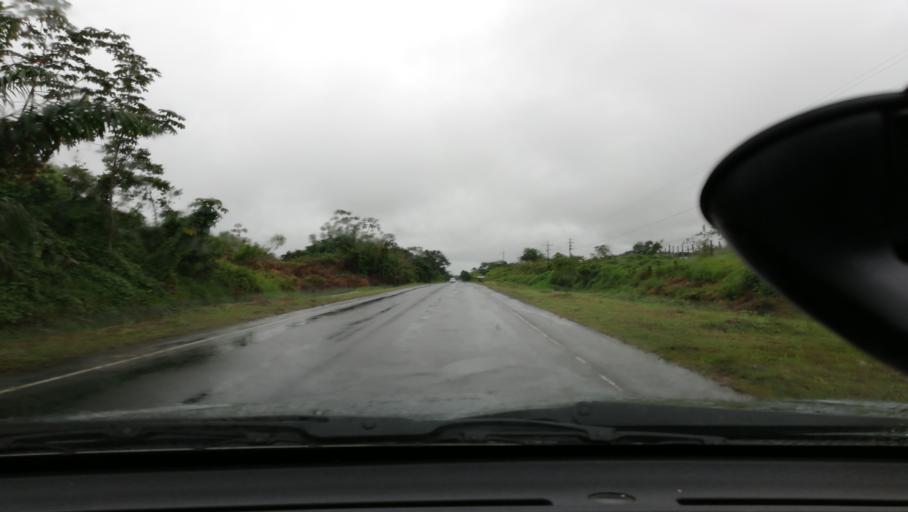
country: PE
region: Loreto
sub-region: Provincia de Maynas
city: San Juan
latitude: -4.0557
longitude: -73.4391
